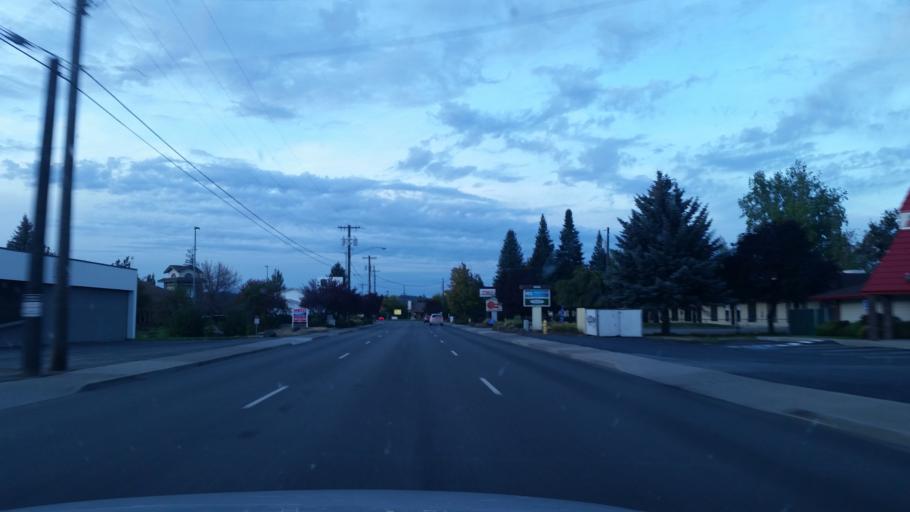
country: US
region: Washington
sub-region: Spokane County
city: Dishman
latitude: 47.6610
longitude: -117.2815
